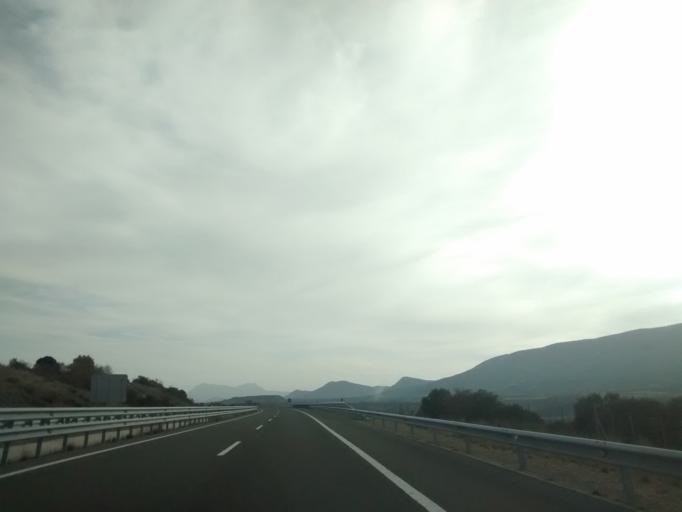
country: ES
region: Aragon
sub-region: Provincia de Zaragoza
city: Artieda
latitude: 42.6106
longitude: -0.9857
